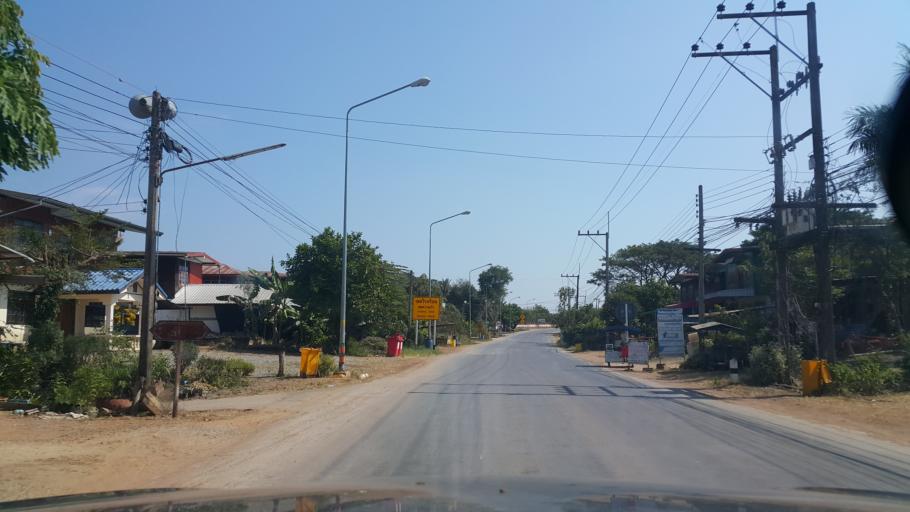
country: TH
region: Changwat Udon Thani
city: Nam Som
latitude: 17.7816
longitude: 102.1278
